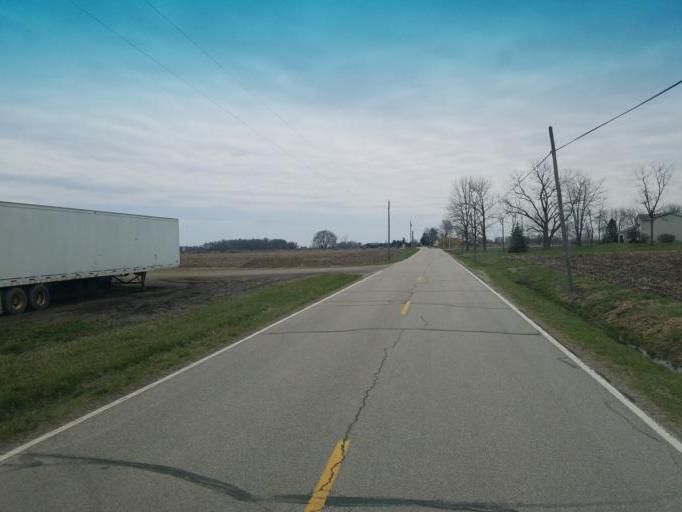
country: US
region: Ohio
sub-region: Crawford County
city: Bucyrus
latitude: 40.8637
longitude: -82.9570
